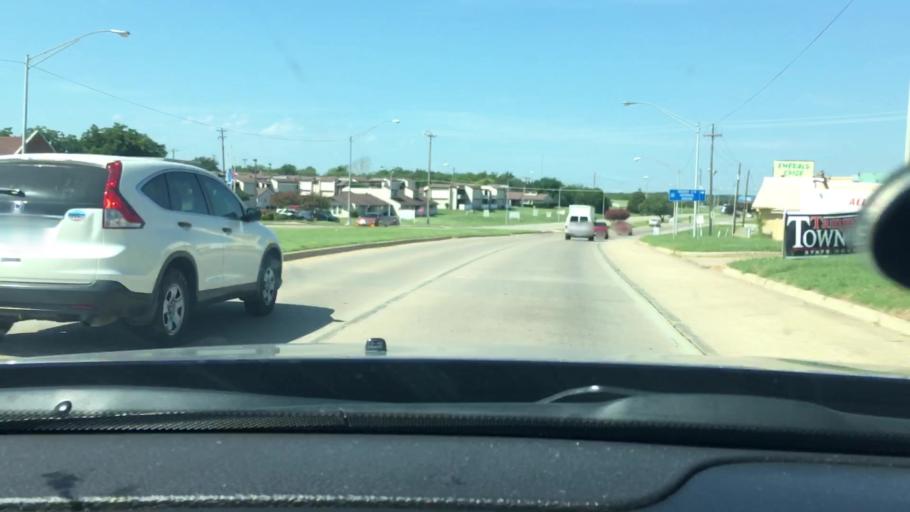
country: US
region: Oklahoma
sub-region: Carter County
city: Ardmore
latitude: 34.1735
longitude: -97.1502
